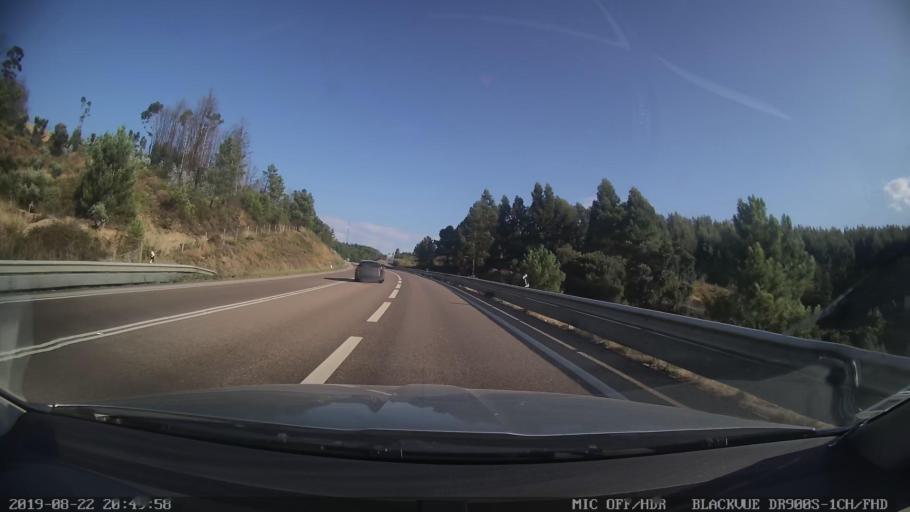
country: PT
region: Castelo Branco
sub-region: Proenca-A-Nova
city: Proenca-a-Nova
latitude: 39.7494
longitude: -7.9346
